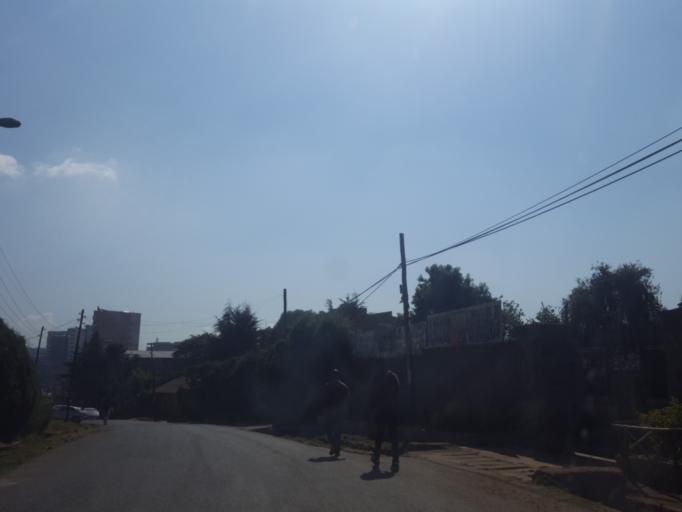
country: ET
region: Adis Abeba
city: Addis Ababa
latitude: 9.0491
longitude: 38.7359
